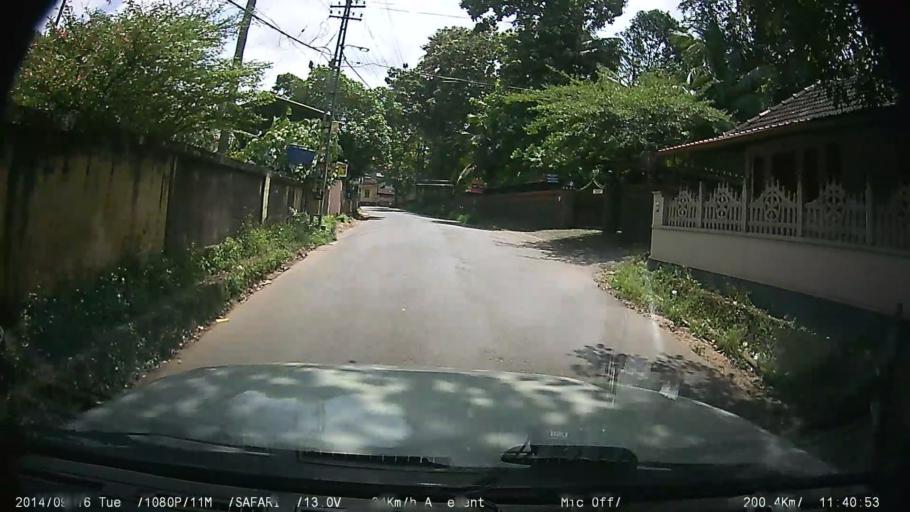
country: IN
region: Kerala
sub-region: Kottayam
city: Changanacheri
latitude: 9.4447
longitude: 76.5511
